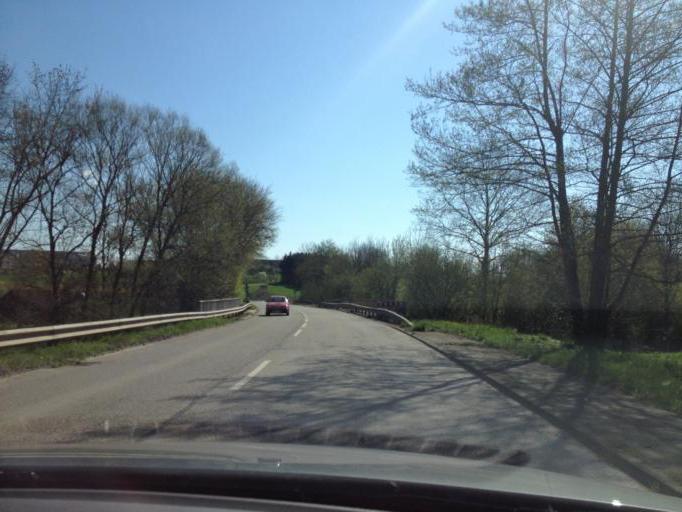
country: DE
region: Baden-Wuerttemberg
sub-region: Regierungsbezirk Stuttgart
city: Neuenstadt am Kocher
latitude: 49.2304
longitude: 9.3427
